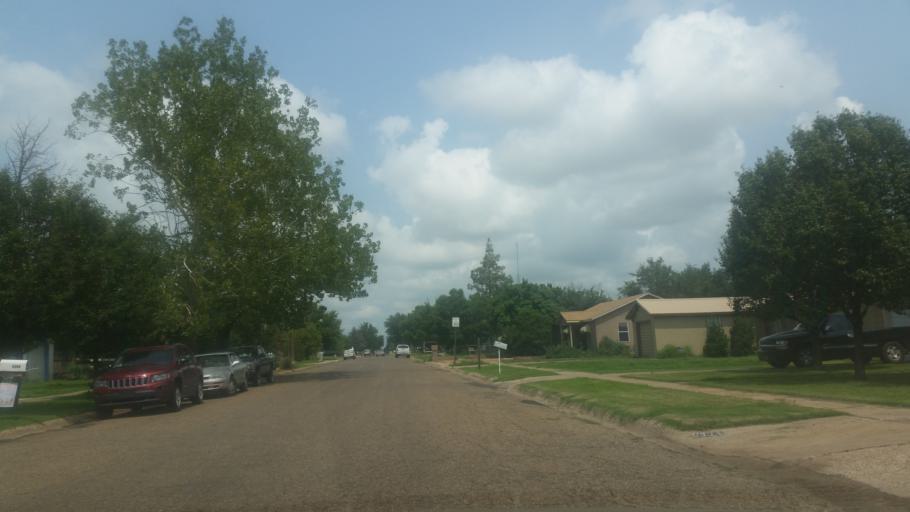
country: US
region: New Mexico
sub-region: Curry County
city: Clovis
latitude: 34.4232
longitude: -103.2015
